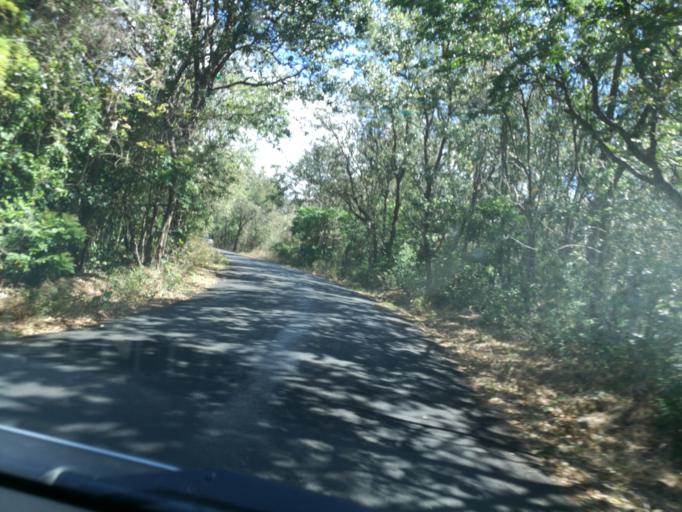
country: CR
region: Guanacaste
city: Liberia
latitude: 10.7467
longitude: -85.3766
